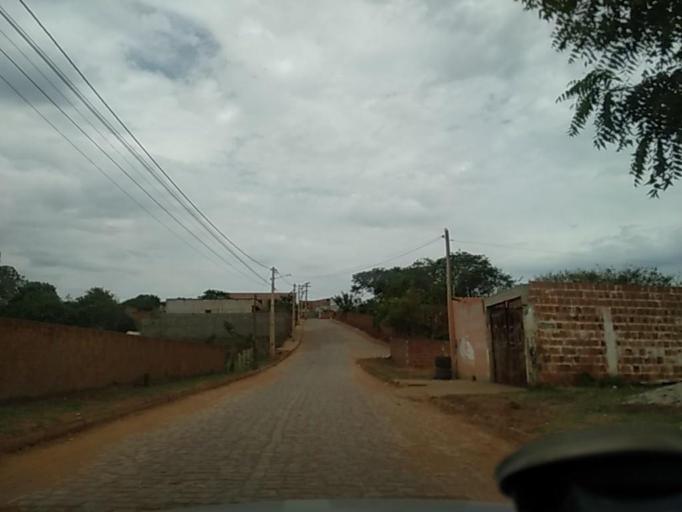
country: BR
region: Bahia
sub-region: Caetite
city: Caetite
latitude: -14.0536
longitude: -42.4784
